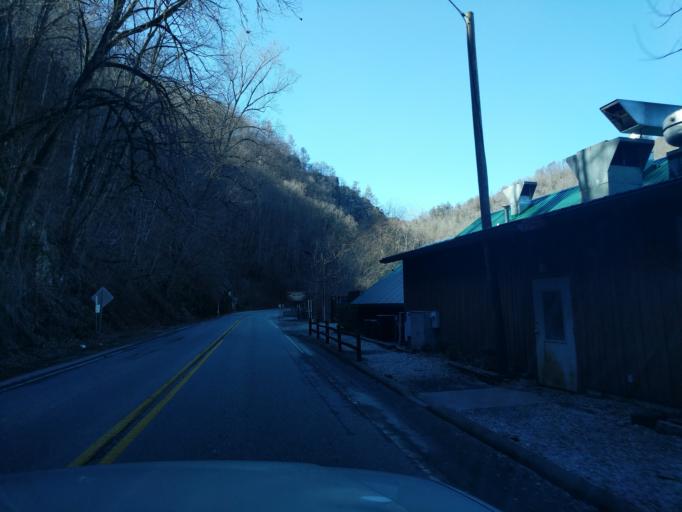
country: US
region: North Carolina
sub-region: Swain County
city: Bryson City
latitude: 35.3311
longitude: -83.5917
